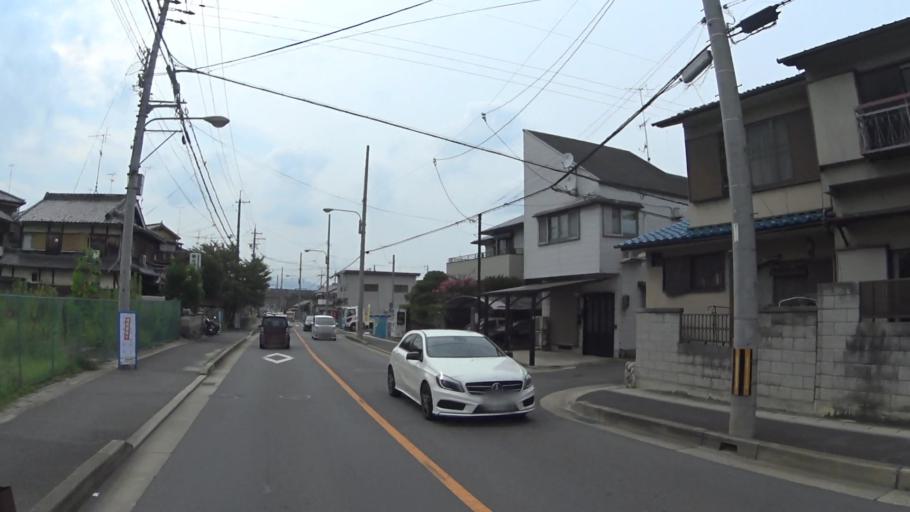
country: JP
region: Kyoto
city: Uji
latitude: 34.9545
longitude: 135.7796
